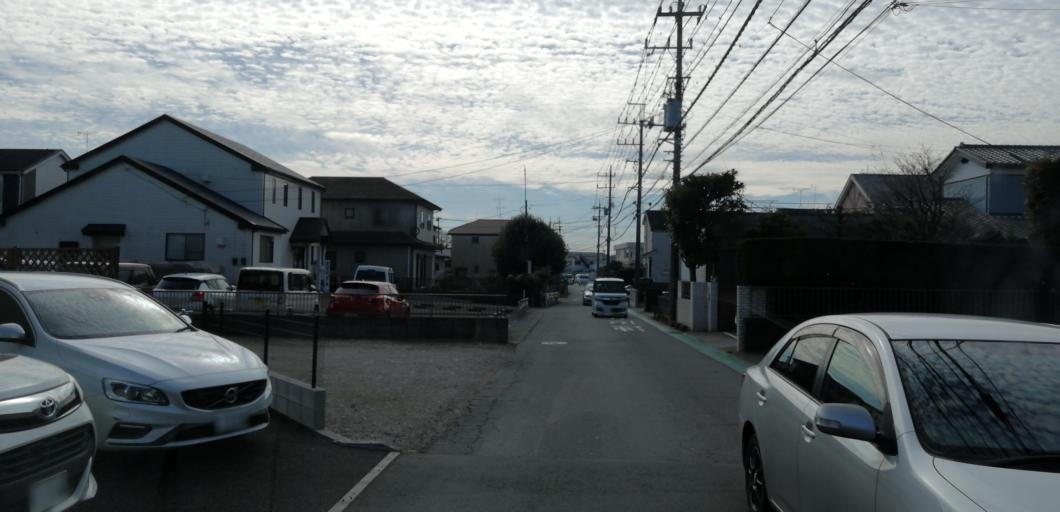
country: JP
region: Chiba
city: Narita
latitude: 35.7411
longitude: 140.3321
